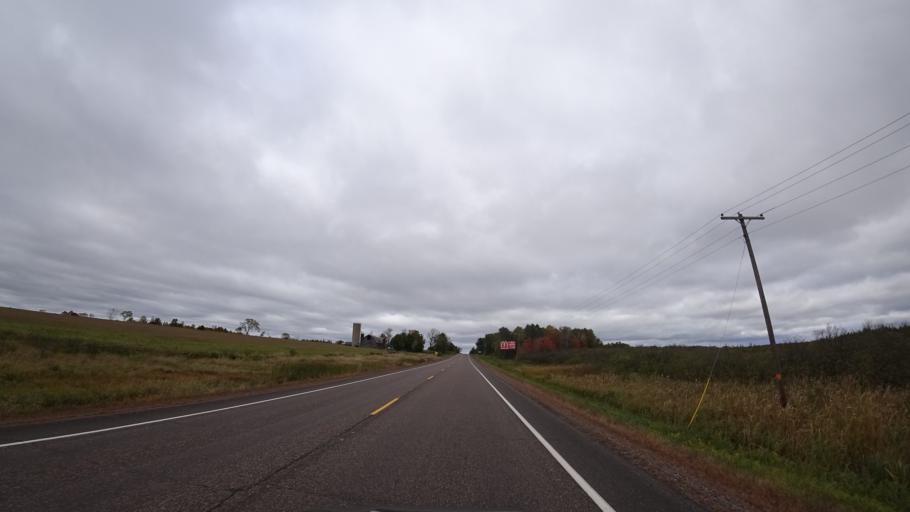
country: US
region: Wisconsin
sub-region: Rusk County
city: Ladysmith
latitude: 45.3658
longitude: -91.1106
